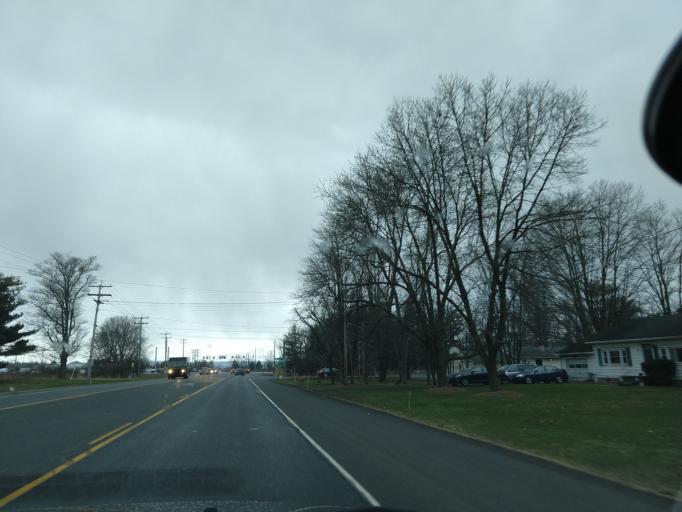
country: US
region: New York
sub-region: Tompkins County
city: Lansing
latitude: 42.4842
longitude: -76.4674
